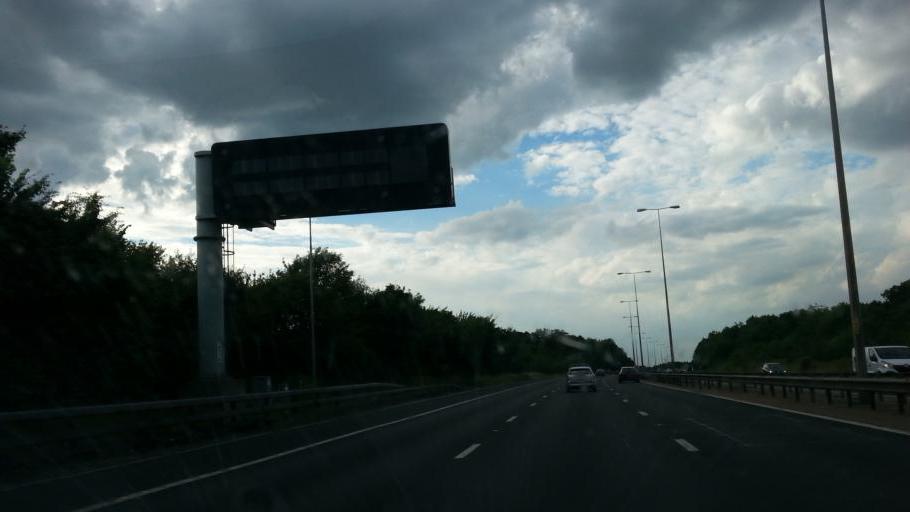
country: GB
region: England
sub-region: Worcestershire
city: Upton upon Severn
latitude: 52.0941
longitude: -2.1840
